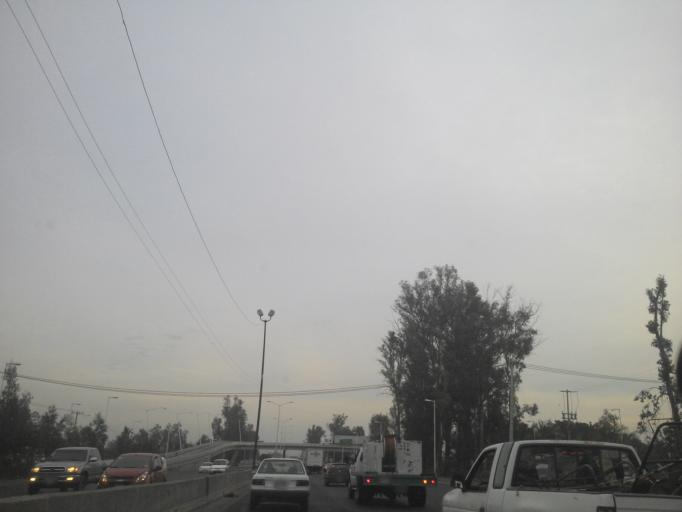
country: MX
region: Jalisco
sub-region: Tlajomulco de Zuniga
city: Palomar
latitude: 20.6396
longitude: -103.4398
